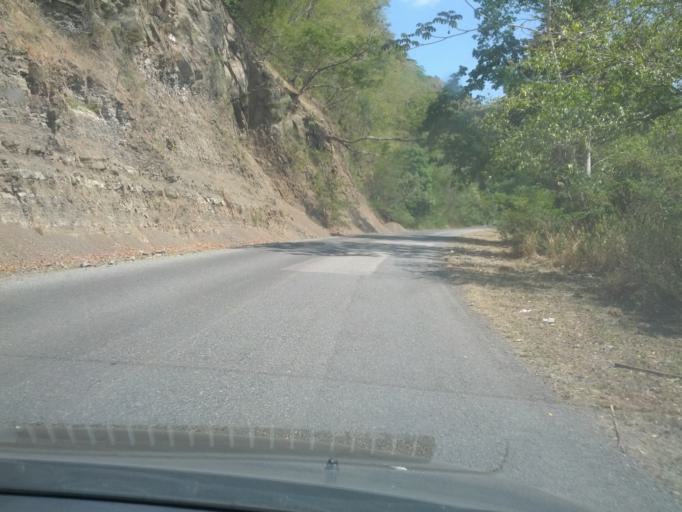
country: CR
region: Puntarenas
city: Ciudad Cortes
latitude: 8.9638
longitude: -83.3182
